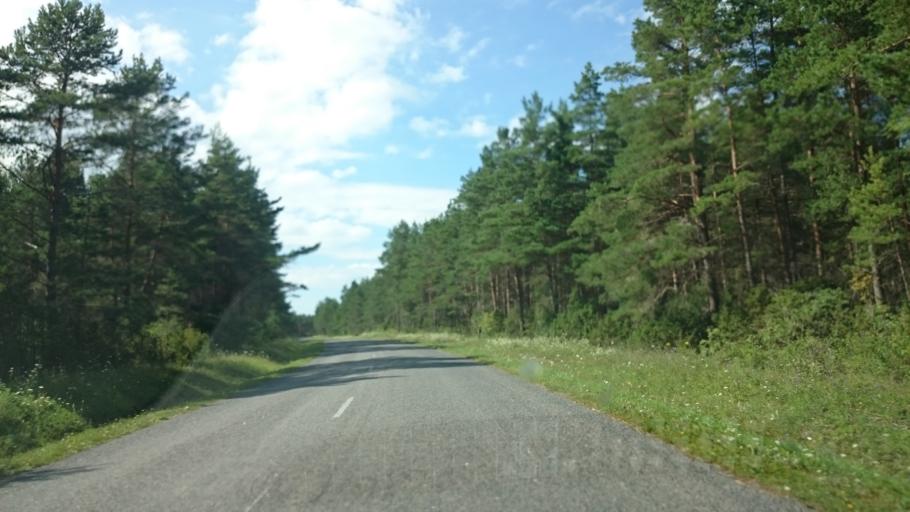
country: EE
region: Saare
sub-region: Orissaare vald
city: Orissaare
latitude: 58.5905
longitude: 23.0144
